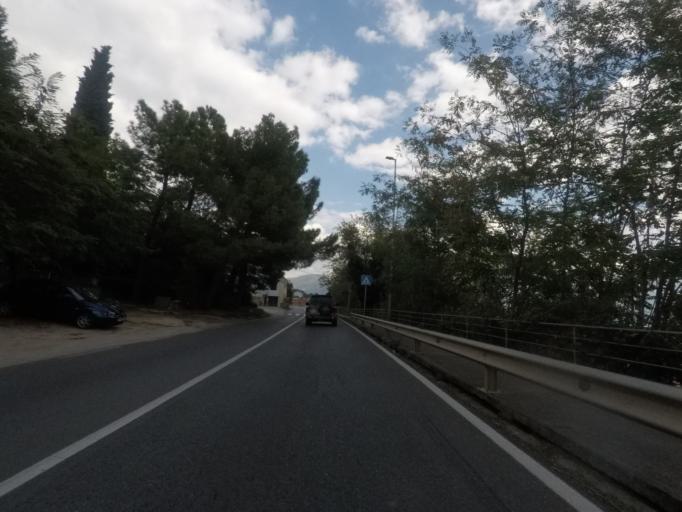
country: ME
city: Bijela
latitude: 42.4392
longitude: 18.6131
